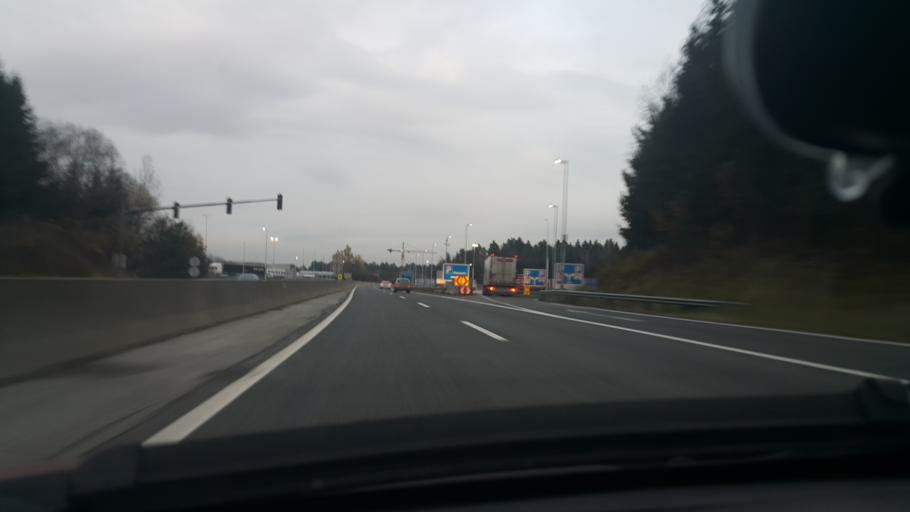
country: AT
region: Carinthia
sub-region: Politischer Bezirk Klagenfurt Land
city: Poggersdorf
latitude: 46.6402
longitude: 14.4353
